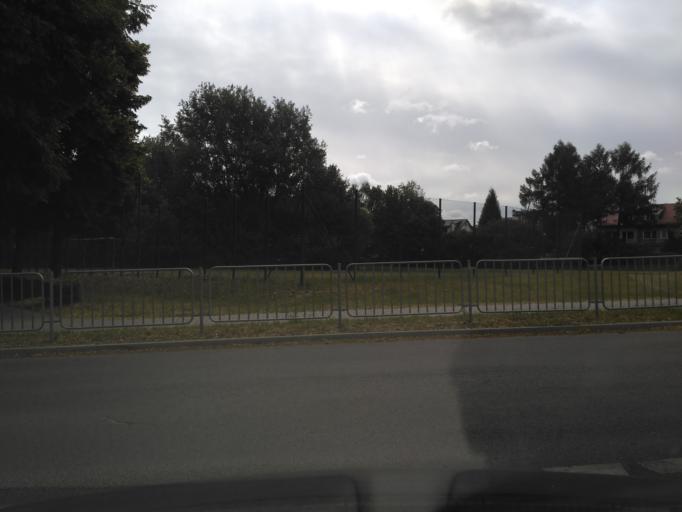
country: PL
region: Lublin Voivodeship
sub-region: Powiat lubelski
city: Lublin
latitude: 51.2277
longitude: 22.5347
